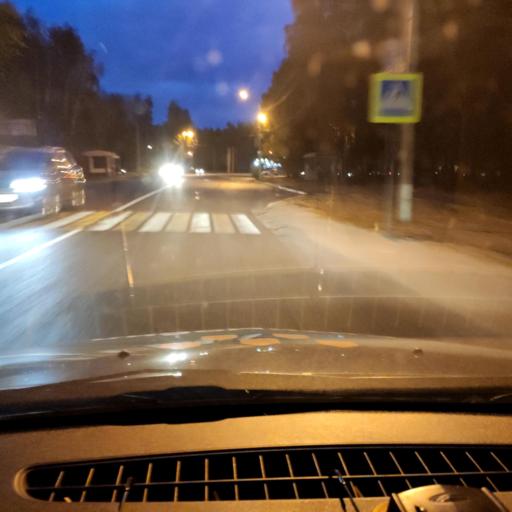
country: RU
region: Voronezj
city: Pridonskoy
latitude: 51.6886
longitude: 39.1023
